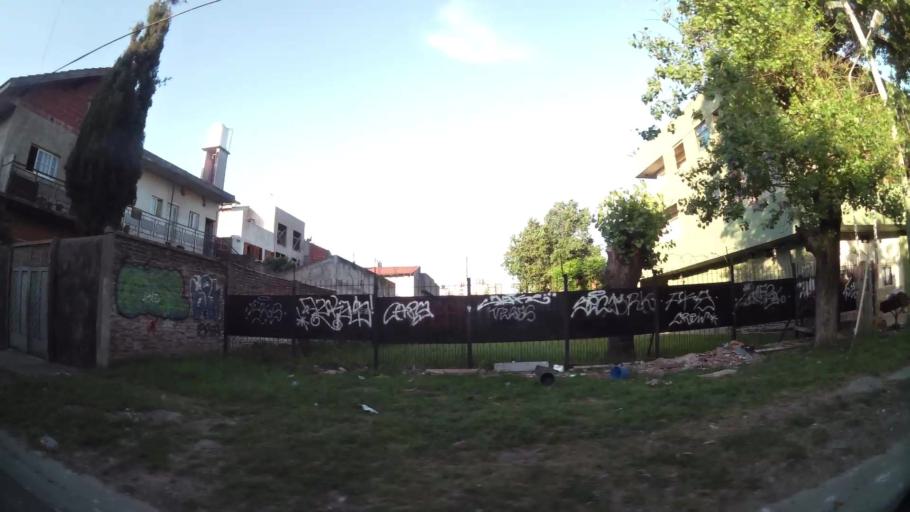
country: AR
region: Buenos Aires F.D.
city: Villa Lugano
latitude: -34.6961
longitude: -58.4807
